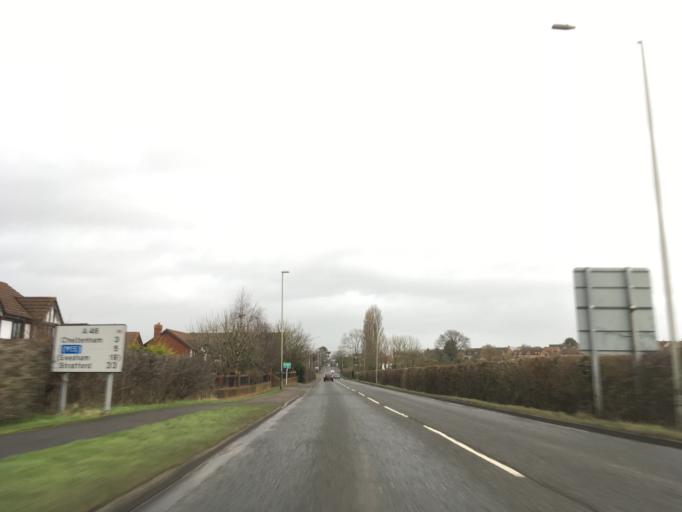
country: GB
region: England
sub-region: Gloucestershire
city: Shurdington
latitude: 51.8771
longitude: -2.1007
